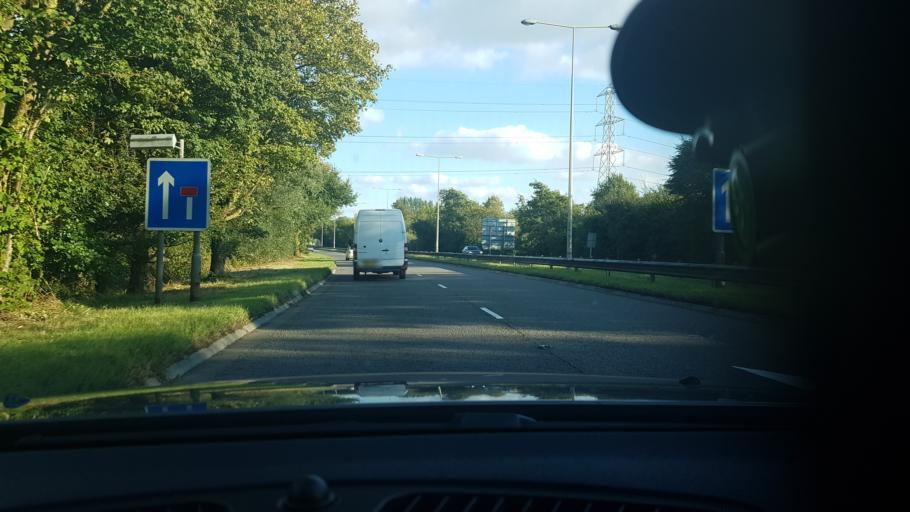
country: GB
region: England
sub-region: Gloucestershire
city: Cirencester
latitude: 51.7067
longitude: -1.9513
